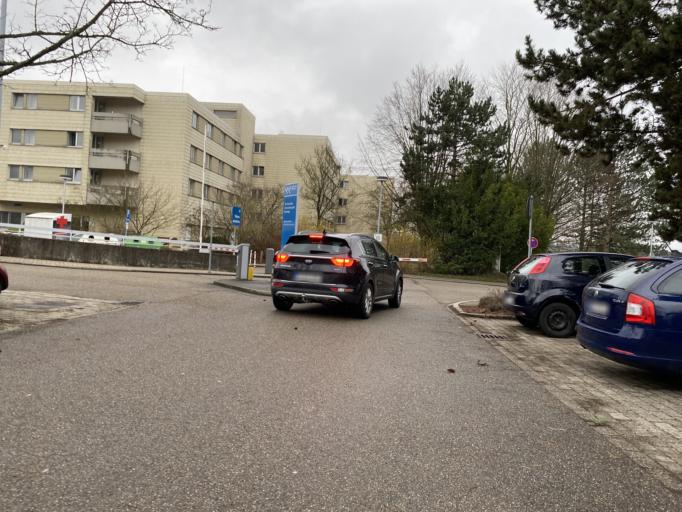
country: DE
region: Baden-Wuerttemberg
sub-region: Karlsruhe Region
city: Muhlacker
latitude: 48.9508
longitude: 8.8582
